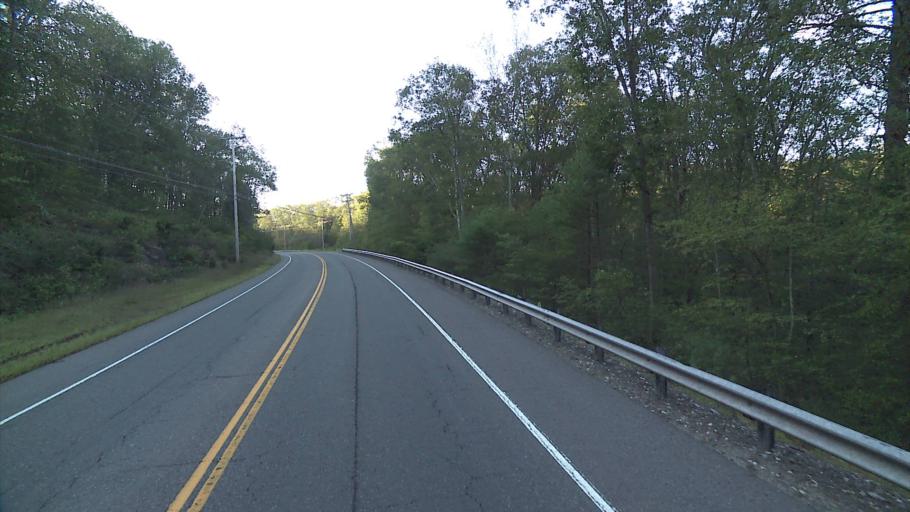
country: US
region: Connecticut
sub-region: Tolland County
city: Stafford Springs
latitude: 41.9253
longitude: -72.3046
